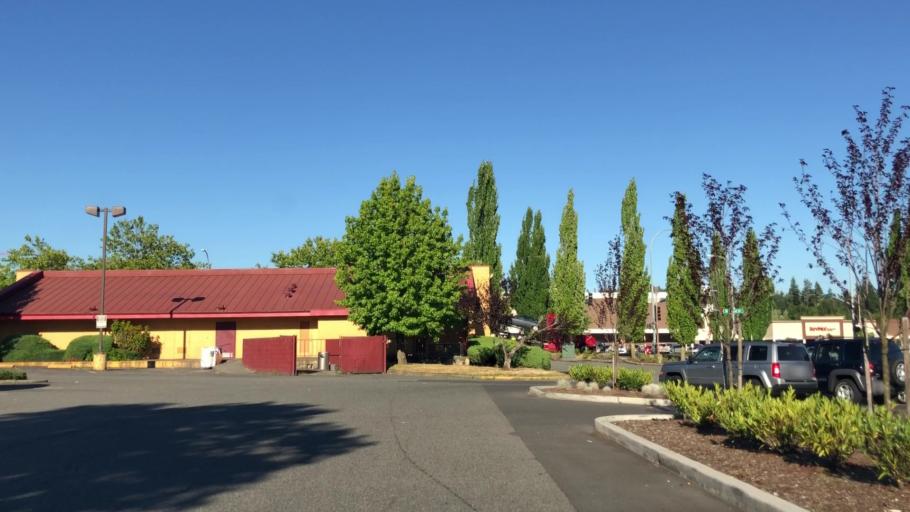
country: US
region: Washington
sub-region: King County
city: Redmond
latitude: 47.6302
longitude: -122.1443
